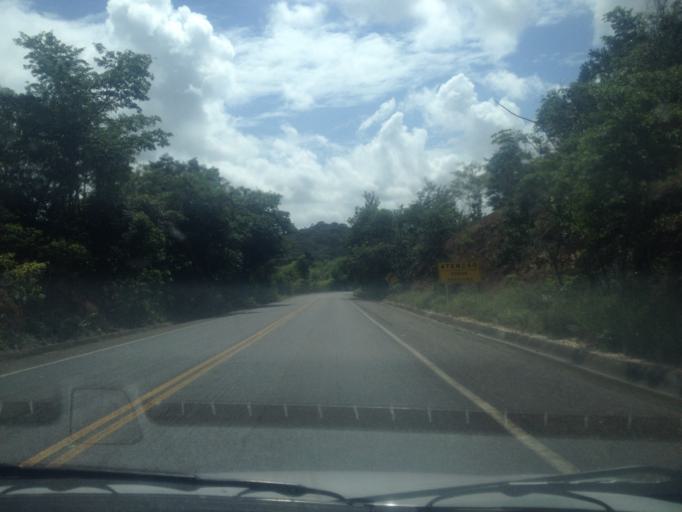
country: BR
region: Bahia
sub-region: Conde
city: Conde
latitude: -12.0417
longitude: -37.7061
